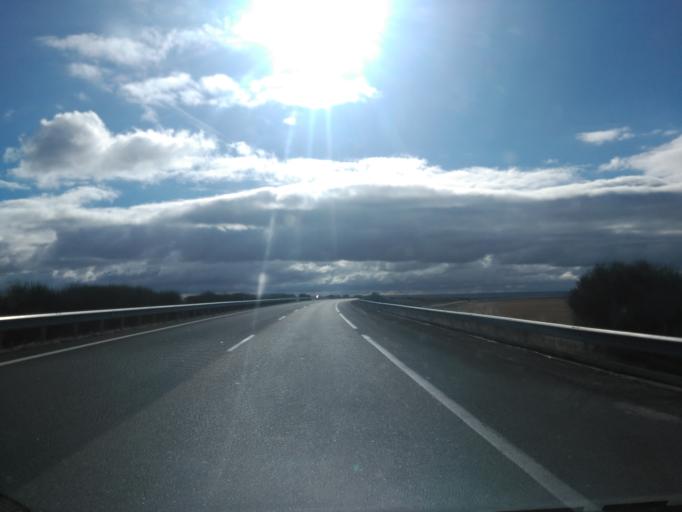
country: ES
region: Castille and Leon
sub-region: Provincia de Palencia
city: Marcilla de Campos
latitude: 42.3083
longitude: -4.3994
